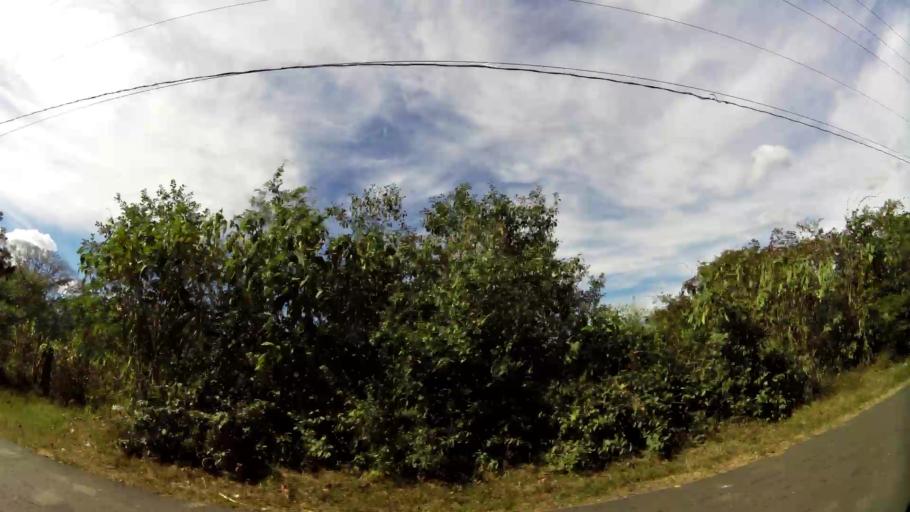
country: SV
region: San Salvador
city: Aguilares
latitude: 13.9570
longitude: -89.1410
